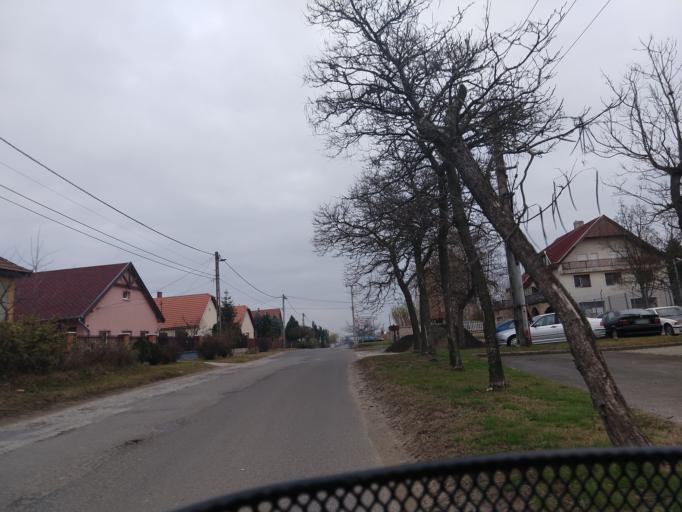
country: HU
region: Pest
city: Veresegyhaz
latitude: 47.6642
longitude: 19.2823
